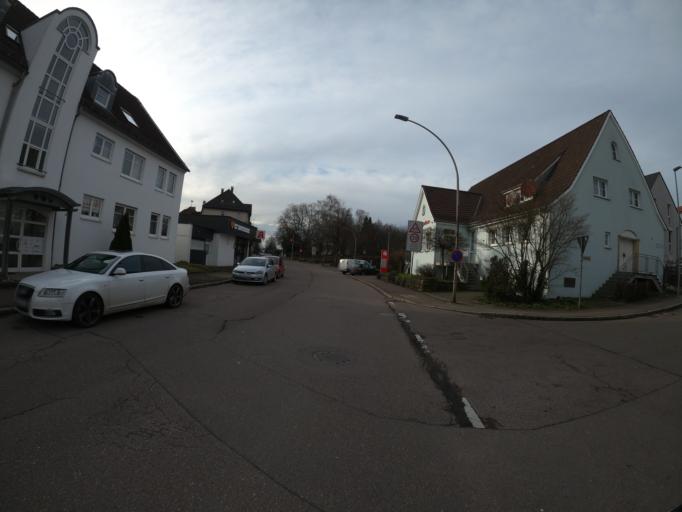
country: DE
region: Baden-Wuerttemberg
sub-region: Regierungsbezirk Stuttgart
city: Rechberghausen
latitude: 48.7241
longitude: 9.6550
